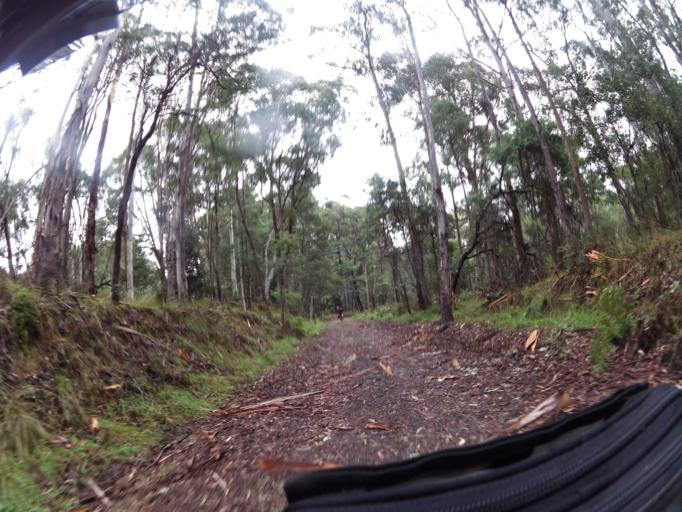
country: AU
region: New South Wales
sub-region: Greater Hume Shire
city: Holbrook
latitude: -36.1475
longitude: 147.4605
